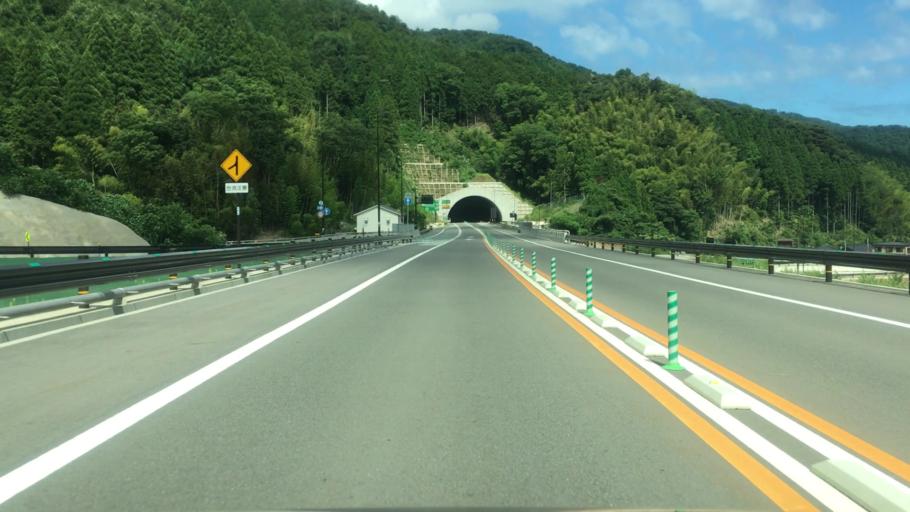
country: JP
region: Hyogo
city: Toyooka
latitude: 35.6384
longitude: 134.5656
